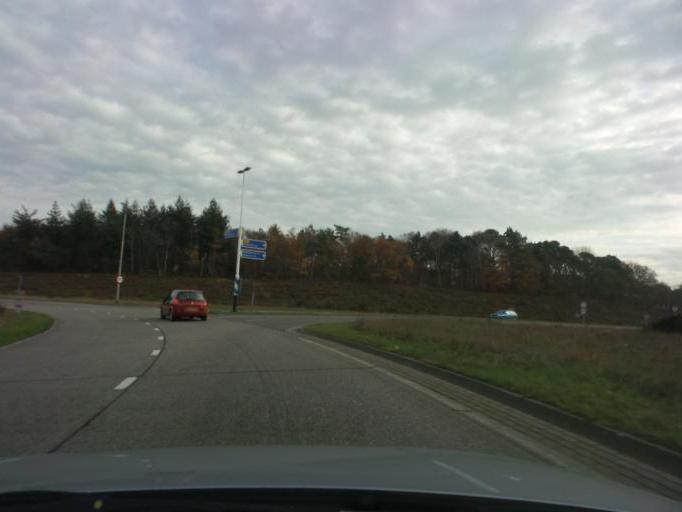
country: NL
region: Utrecht
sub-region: Gemeente Amersfoort
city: Amersfoort
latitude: 52.1389
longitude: 5.3572
